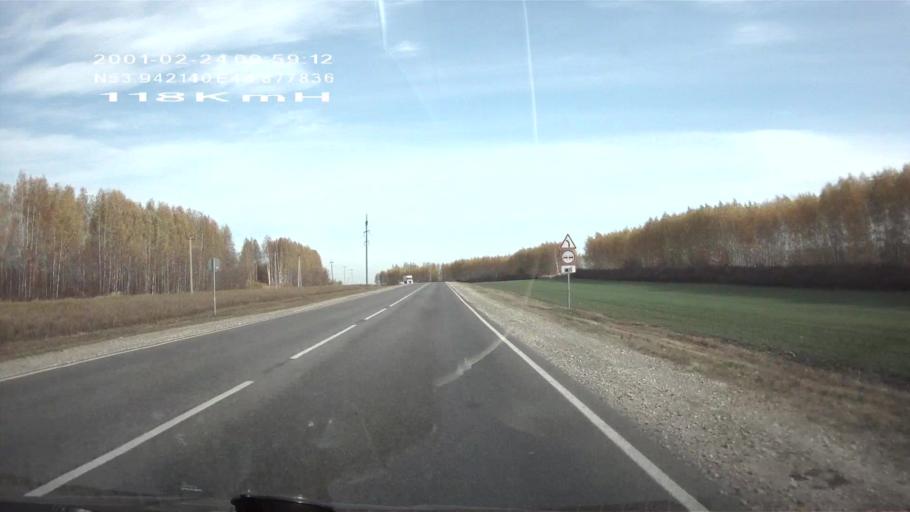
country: RU
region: Penza
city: Issa
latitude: 53.9427
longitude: 44.8783
